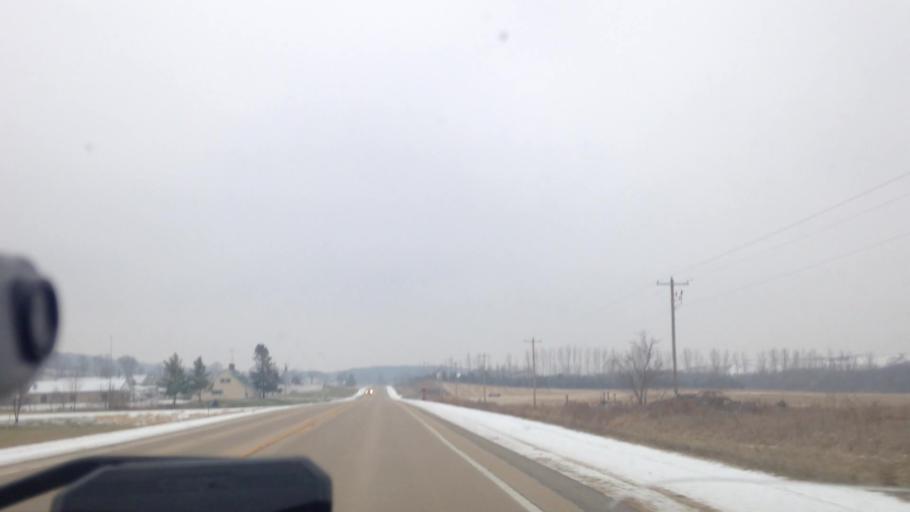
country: US
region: Wisconsin
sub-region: Dodge County
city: Mayville
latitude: 43.4750
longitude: -88.5462
